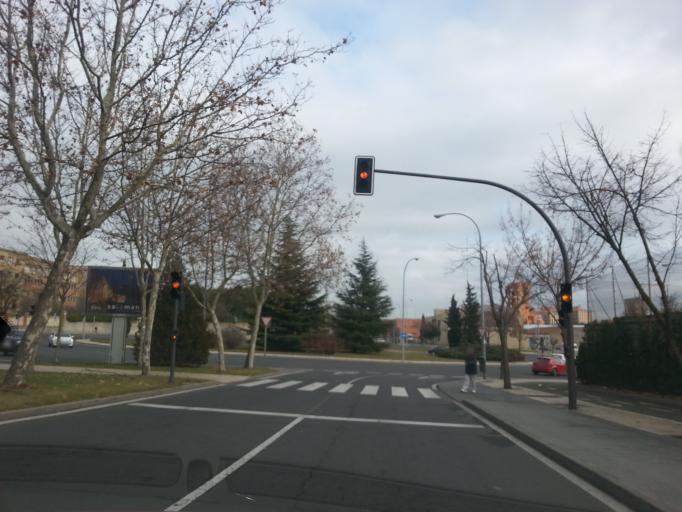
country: ES
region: Castille and Leon
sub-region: Provincia de Salamanca
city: Salamanca
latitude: 40.9789
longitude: -5.6643
